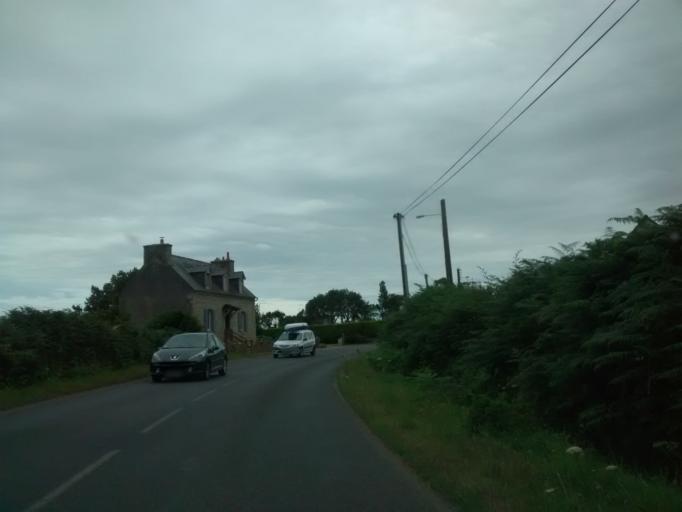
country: FR
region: Brittany
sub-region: Departement des Cotes-d'Armor
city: Trelevern
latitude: 48.8000
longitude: -3.3798
